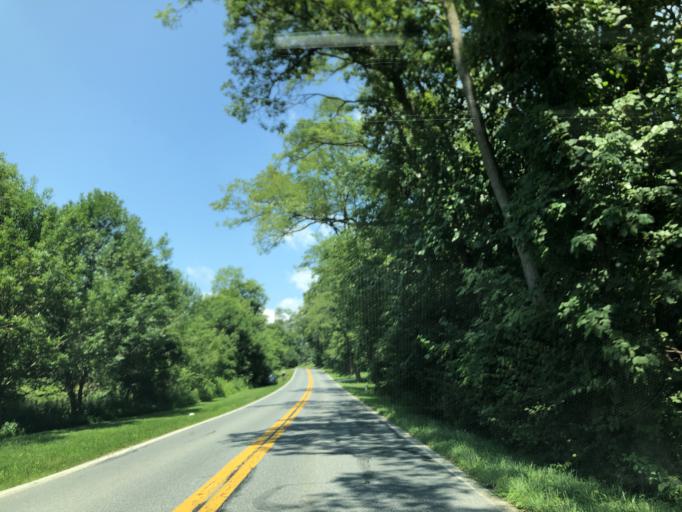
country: US
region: Maryland
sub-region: Carroll County
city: Westminster
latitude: 39.5248
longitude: -76.9519
